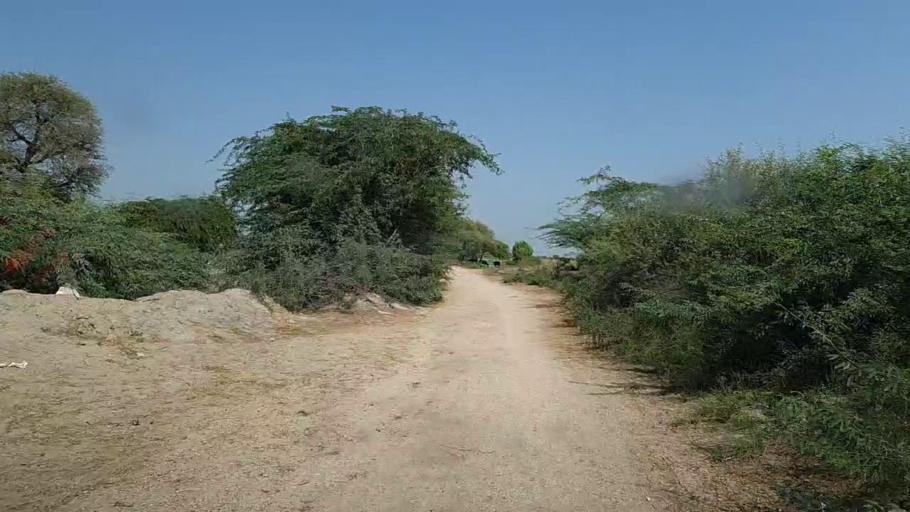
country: PK
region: Sindh
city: Mirpur Batoro
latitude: 24.7104
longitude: 68.4202
